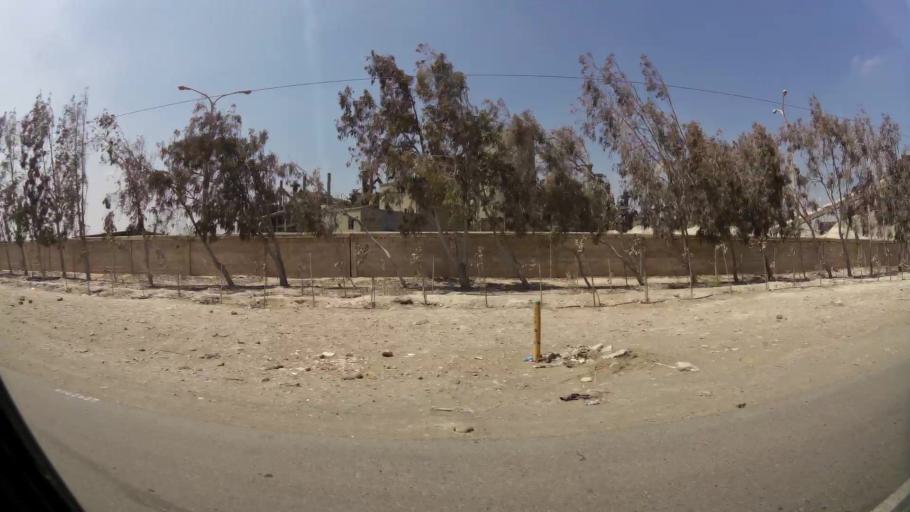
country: PE
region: La Libertad
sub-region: Provincia de Pacasmayo
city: Pacasmayo
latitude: -7.4070
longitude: -79.5569
